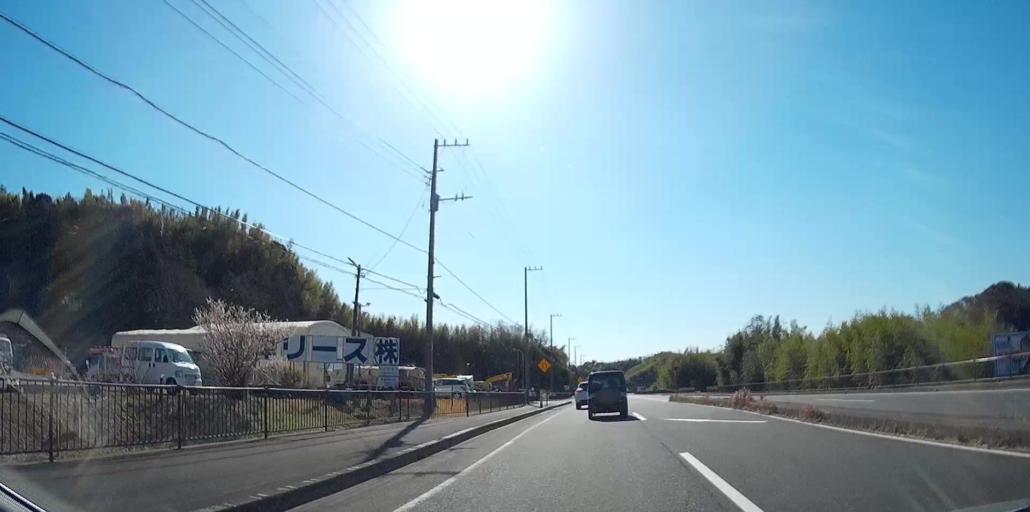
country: JP
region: Chiba
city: Kimitsu
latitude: 35.3026
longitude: 139.9166
